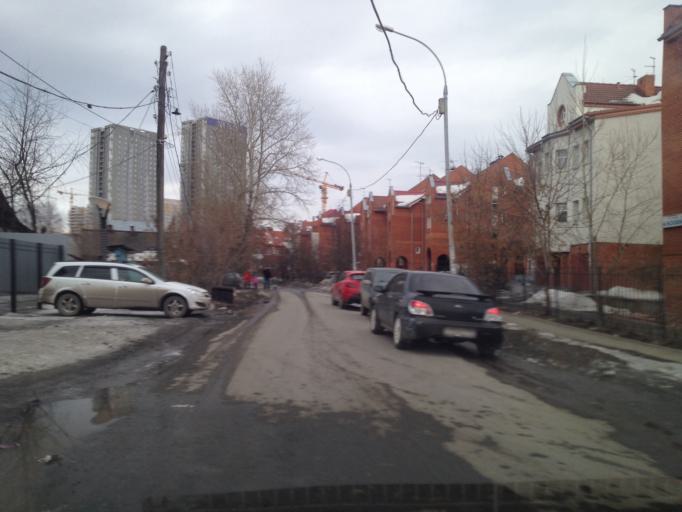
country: RU
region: Sverdlovsk
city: Sovkhoznyy
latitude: 56.8024
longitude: 60.5869
